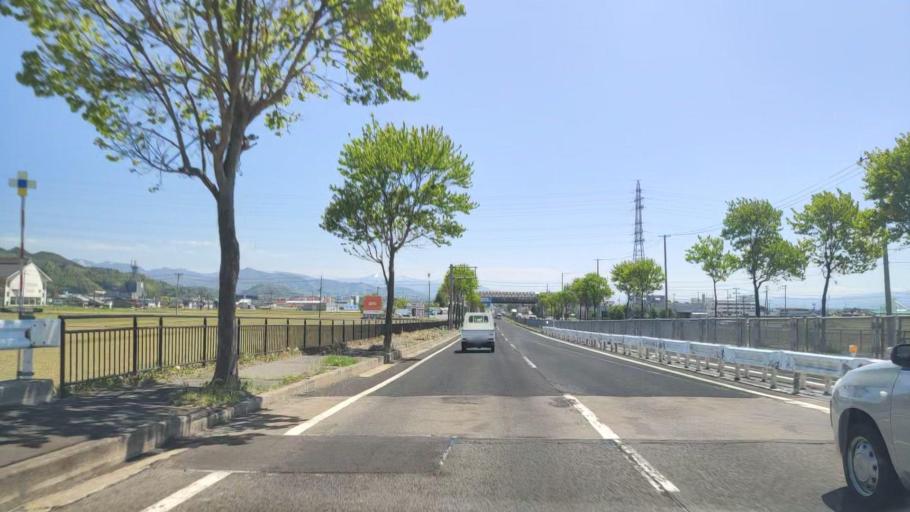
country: JP
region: Yamagata
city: Higashine
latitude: 38.4898
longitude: 140.3832
